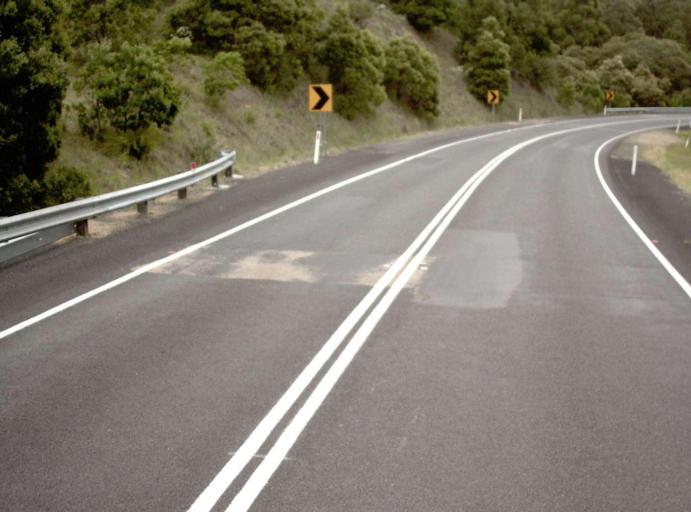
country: AU
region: New South Wales
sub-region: Bombala
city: Bombala
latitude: -37.2418
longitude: 149.2601
